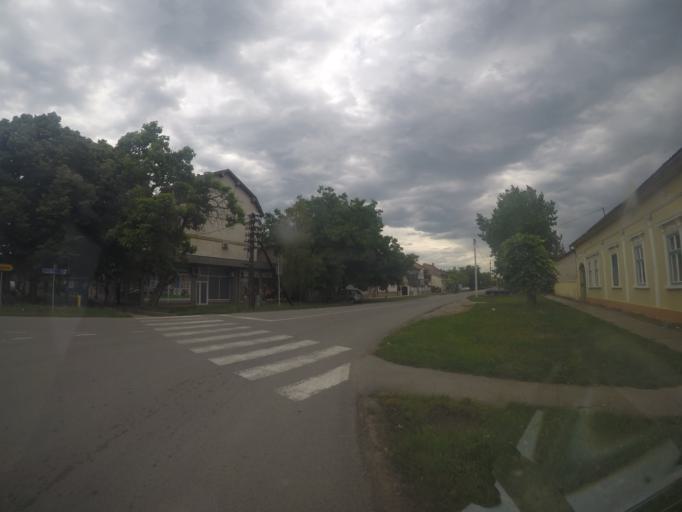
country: RS
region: Autonomna Pokrajina Vojvodina
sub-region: Juznobanatski Okrug
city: Opovo
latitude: 45.0525
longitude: 20.4246
